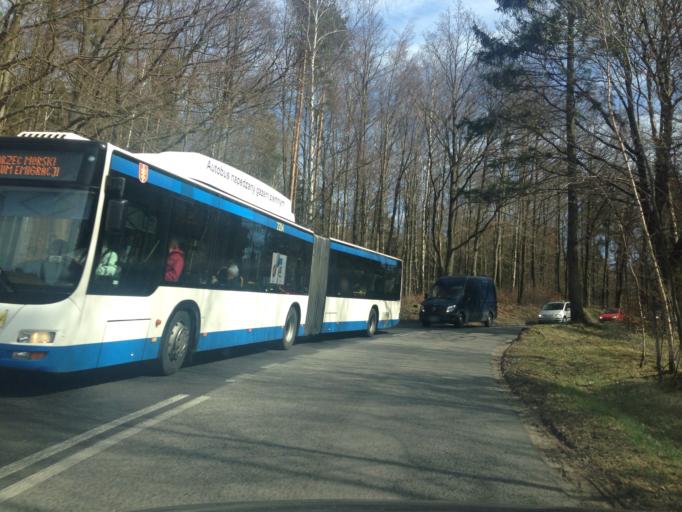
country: PL
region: Pomeranian Voivodeship
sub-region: Gdynia
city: Wielki Kack
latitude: 54.4808
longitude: 18.4460
